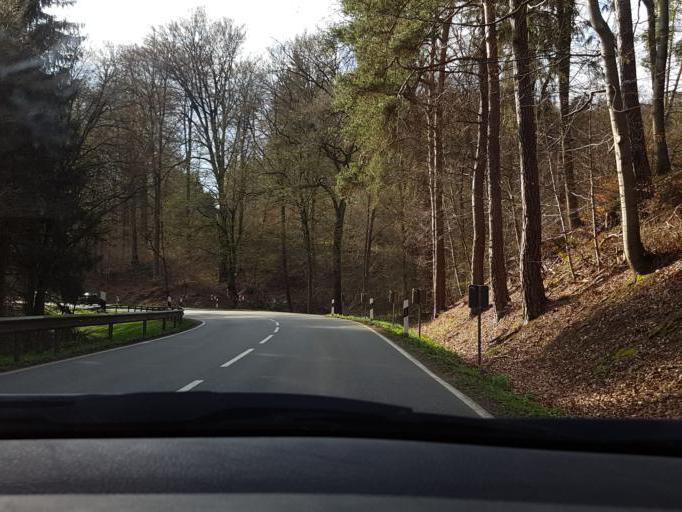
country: DE
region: Lower Saxony
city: Uslar
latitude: 51.6286
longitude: 9.6038
